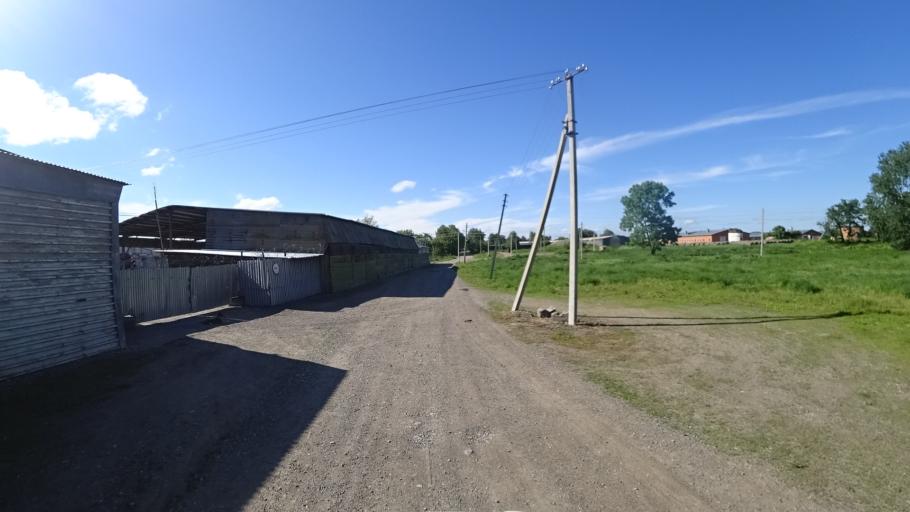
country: RU
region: Khabarovsk Krai
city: Khor
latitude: 47.8864
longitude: 134.9989
